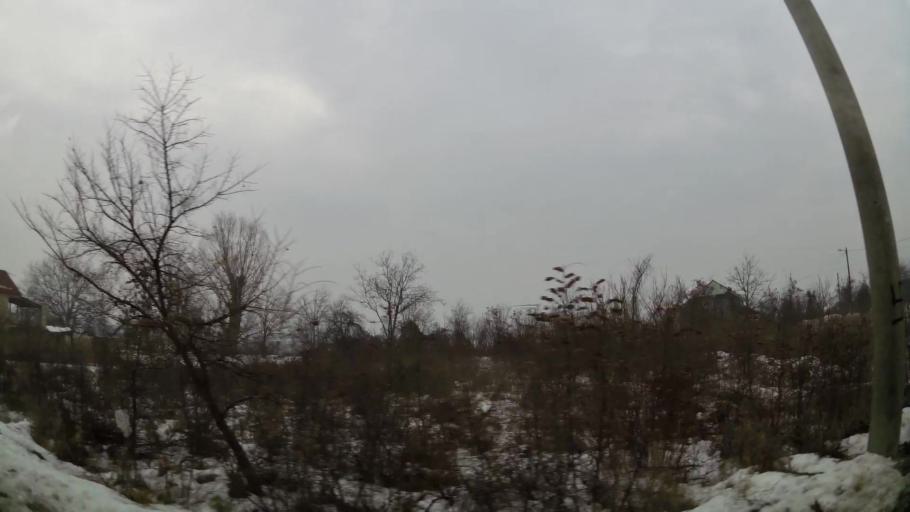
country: MK
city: Kondovo
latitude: 42.0533
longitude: 21.3487
